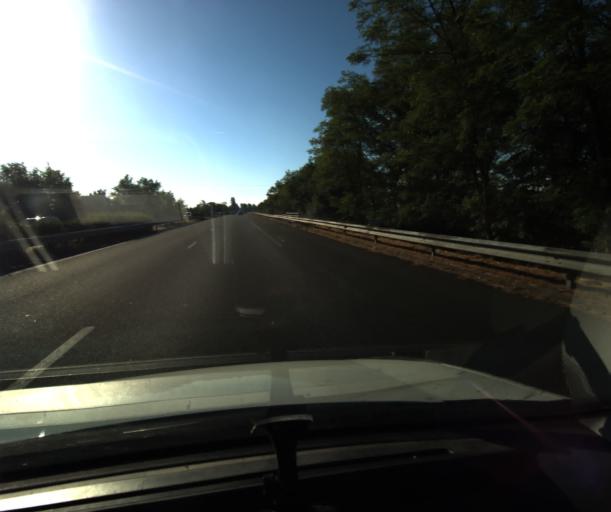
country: FR
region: Midi-Pyrenees
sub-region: Departement du Tarn-et-Garonne
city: Castelsarrasin
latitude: 44.0550
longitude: 1.1248
